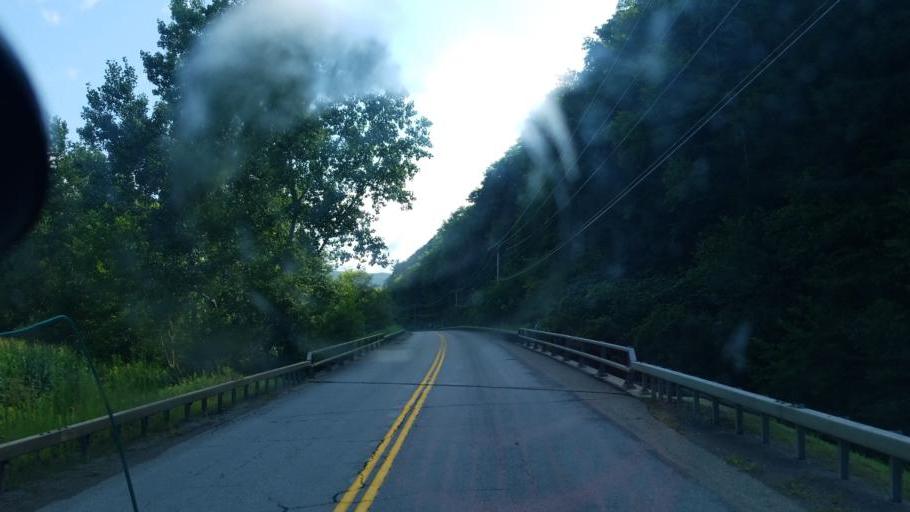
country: US
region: New York
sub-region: Steuben County
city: Canisteo
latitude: 42.2578
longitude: -77.6257
